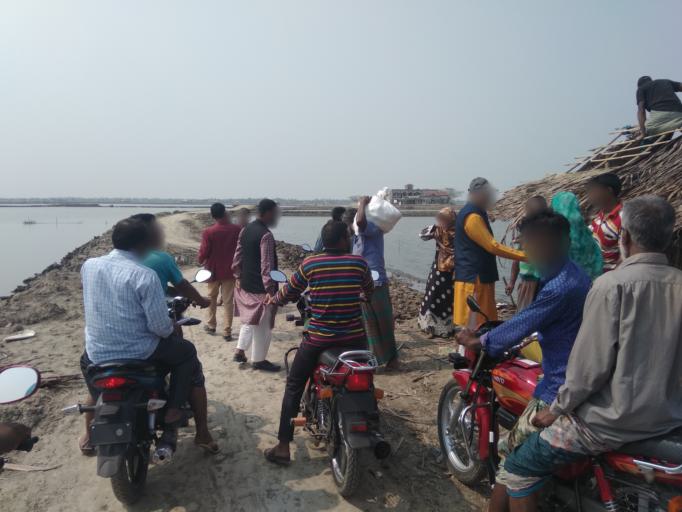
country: IN
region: West Bengal
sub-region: North 24 Parganas
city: Taki
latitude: 22.3443
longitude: 89.2309
